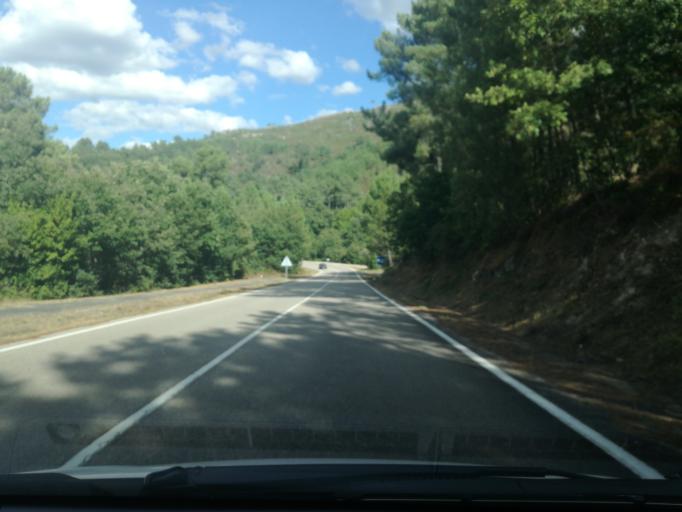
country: ES
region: Galicia
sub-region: Provincia de Ourense
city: Lobios
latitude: 41.8873
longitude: -8.0933
